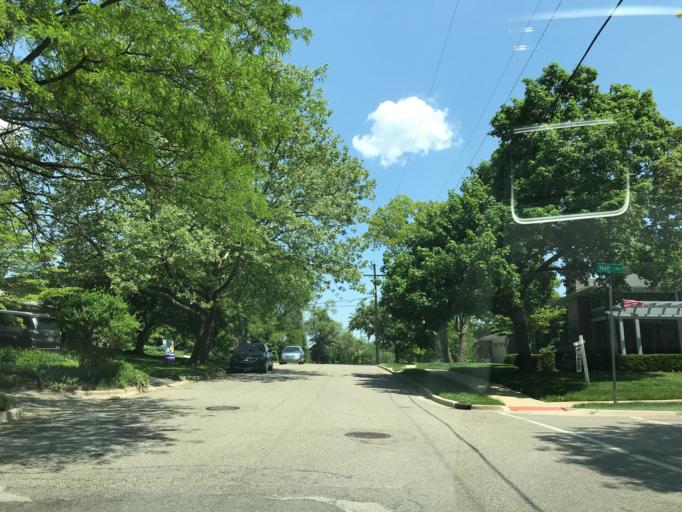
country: US
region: Michigan
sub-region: Washtenaw County
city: Ann Arbor
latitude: 42.2591
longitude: -83.7198
